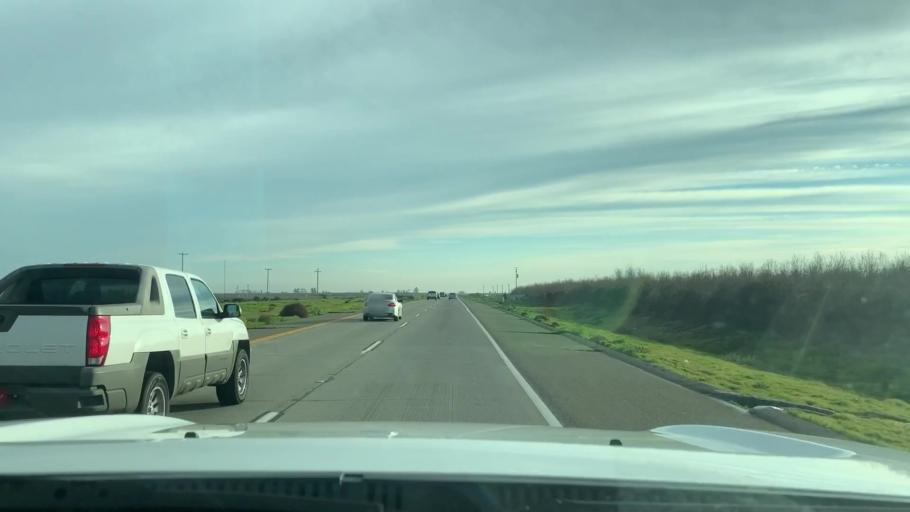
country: US
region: California
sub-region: Fresno County
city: Caruthers
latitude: 36.5317
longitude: -119.7864
